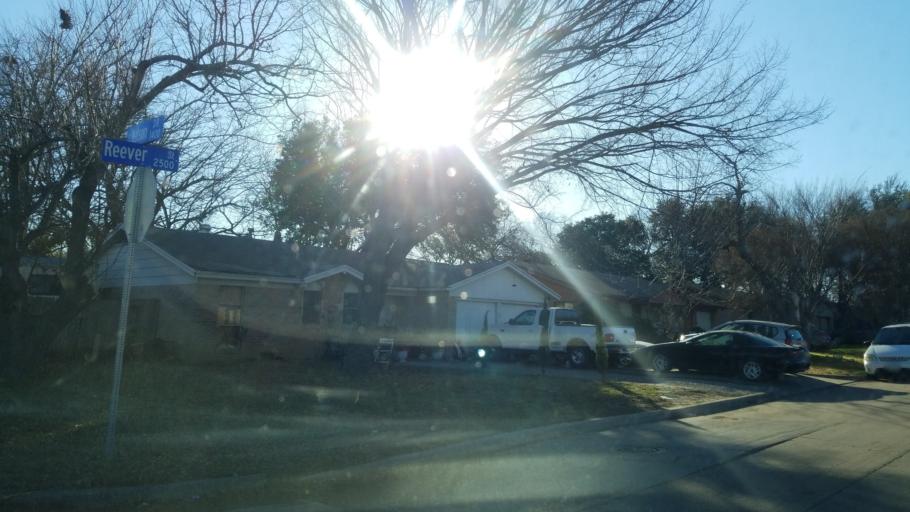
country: US
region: Texas
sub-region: Tarrant County
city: Arlington
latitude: 32.7224
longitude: -97.0632
